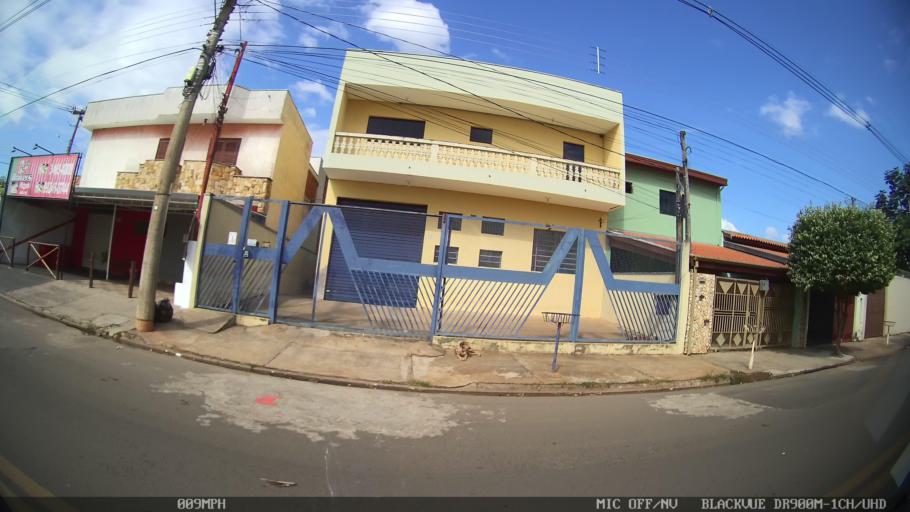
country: BR
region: Sao Paulo
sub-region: Americana
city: Americana
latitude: -22.7197
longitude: -47.3152
